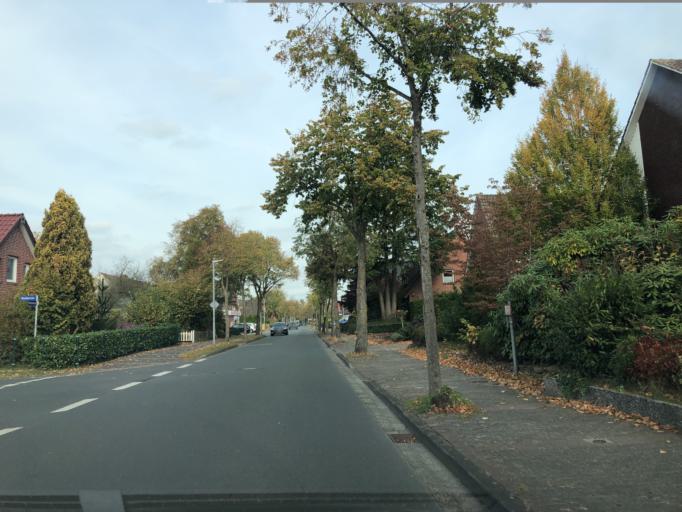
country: DE
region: Lower Saxony
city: Papenburg
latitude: 53.0673
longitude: 7.4081
